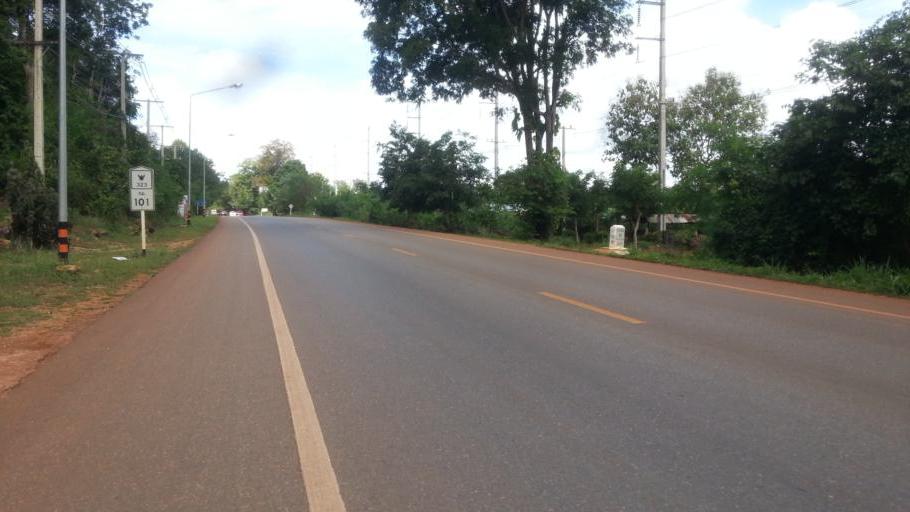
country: TH
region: Kanchanaburi
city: Sai Yok
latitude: 14.1180
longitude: 99.1857
